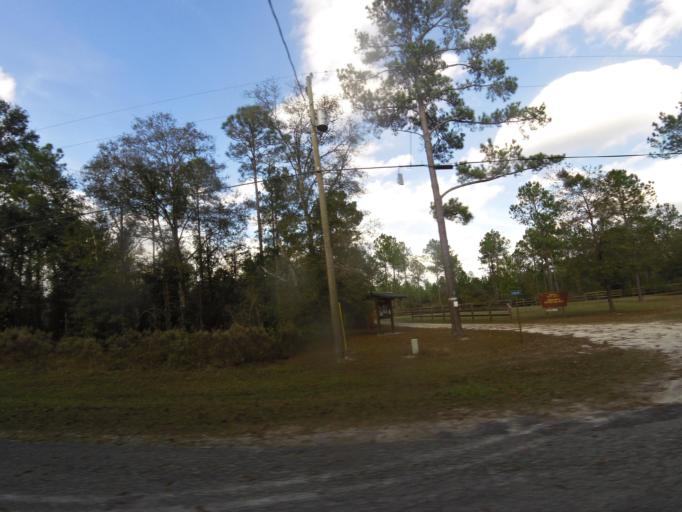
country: US
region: Florida
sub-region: Duval County
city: Baldwin
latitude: 30.1578
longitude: -81.9785
